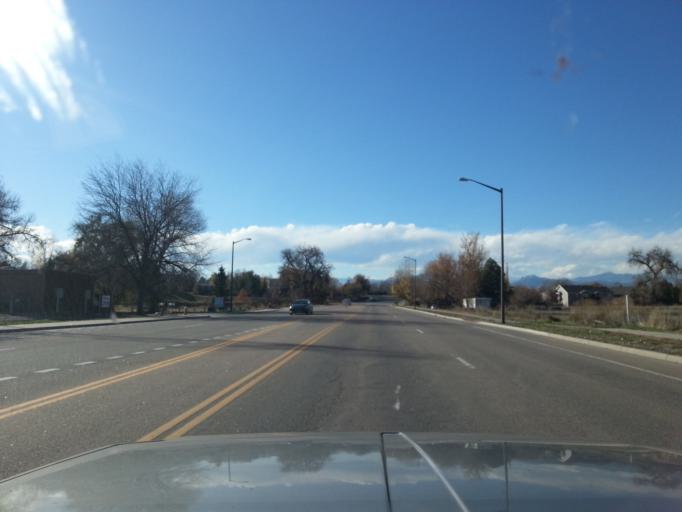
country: US
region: Colorado
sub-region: Larimer County
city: Loveland
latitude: 40.3928
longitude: -105.0983
